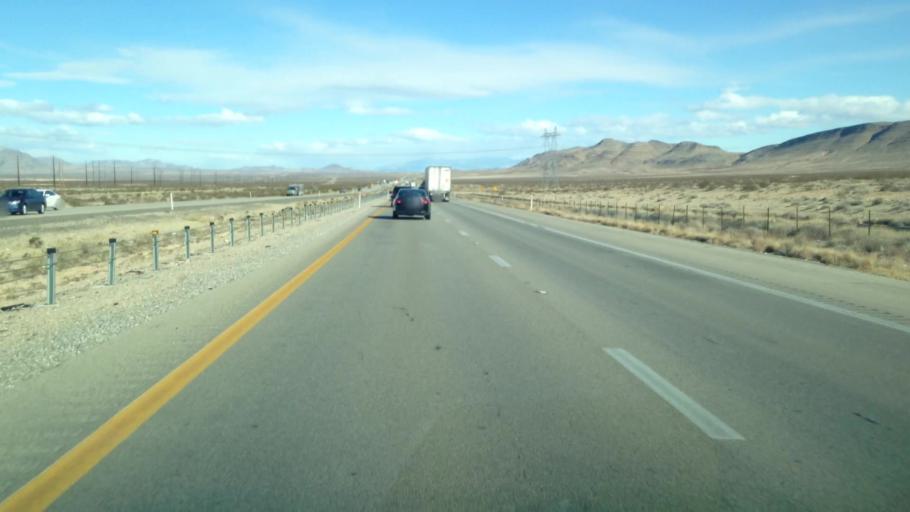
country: US
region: Nevada
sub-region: Clark County
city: Nellis Air Force Base
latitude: 36.3992
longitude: -114.8775
